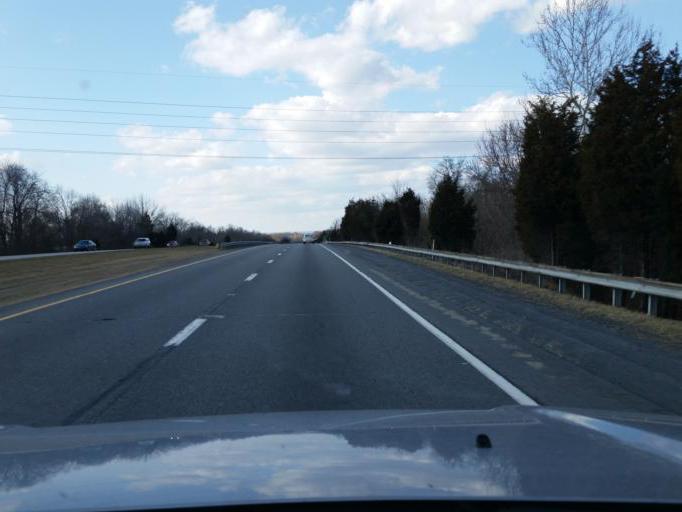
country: US
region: Pennsylvania
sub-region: Dauphin County
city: Middletown
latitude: 40.2076
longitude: -76.7058
